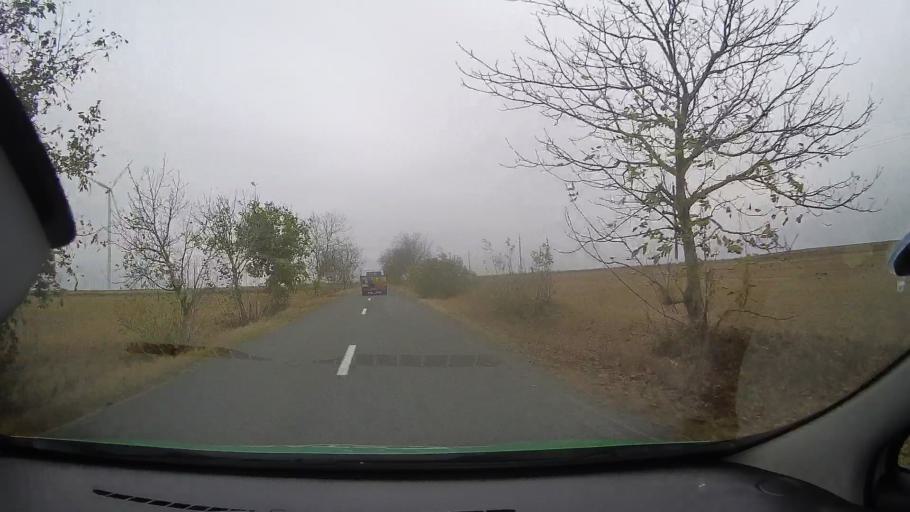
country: RO
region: Constanta
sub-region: Comuna Targusor
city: Targusor
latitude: 44.4782
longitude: 28.3768
